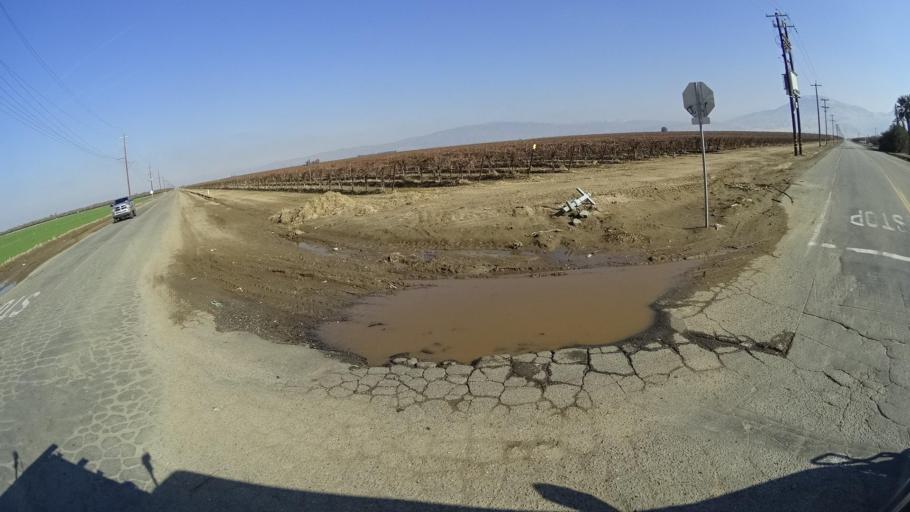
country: US
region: California
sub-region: Kern County
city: Arvin
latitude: 35.1943
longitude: -118.8782
